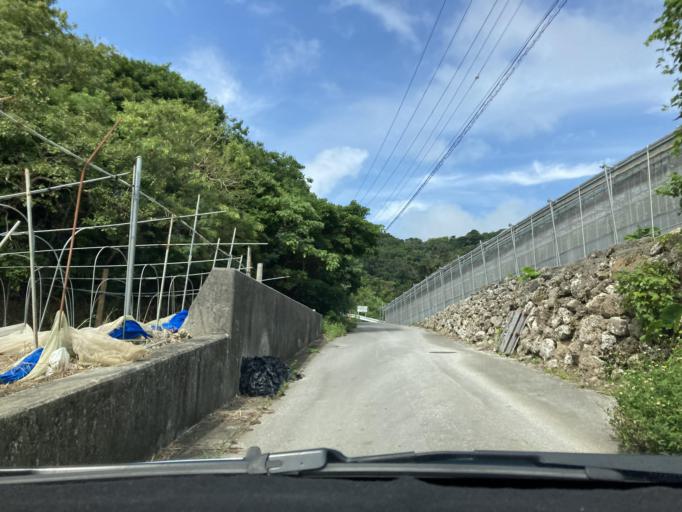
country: JP
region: Okinawa
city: Ginowan
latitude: 26.1594
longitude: 127.8088
